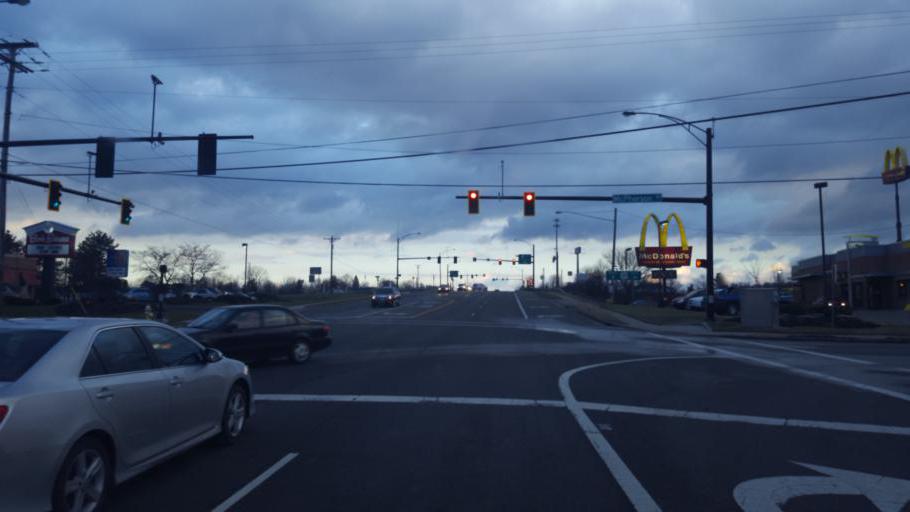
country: US
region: Ohio
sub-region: Richland County
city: Mansfield
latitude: 40.7727
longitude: -82.5516
